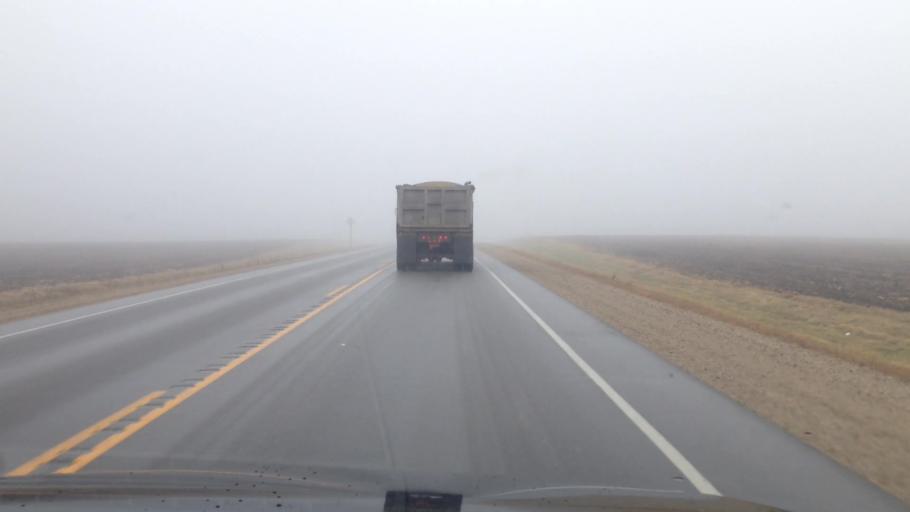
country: US
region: Illinois
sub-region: McHenry County
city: Hebron
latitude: 42.5183
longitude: -88.4427
